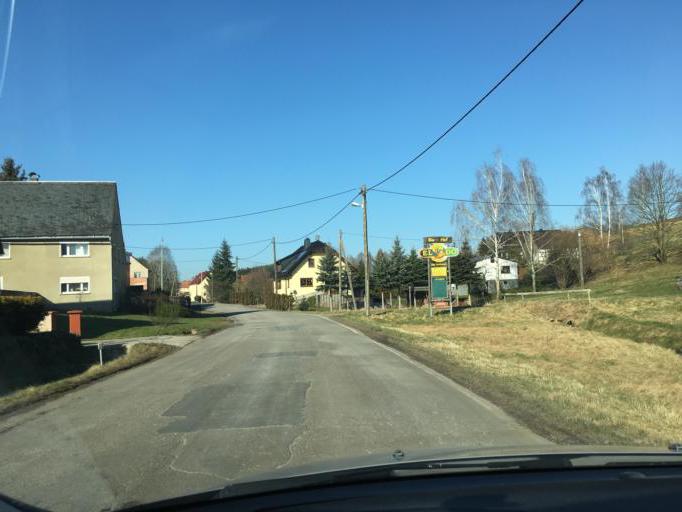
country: DE
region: Saxony
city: Penig
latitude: 50.9699
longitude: 12.7117
